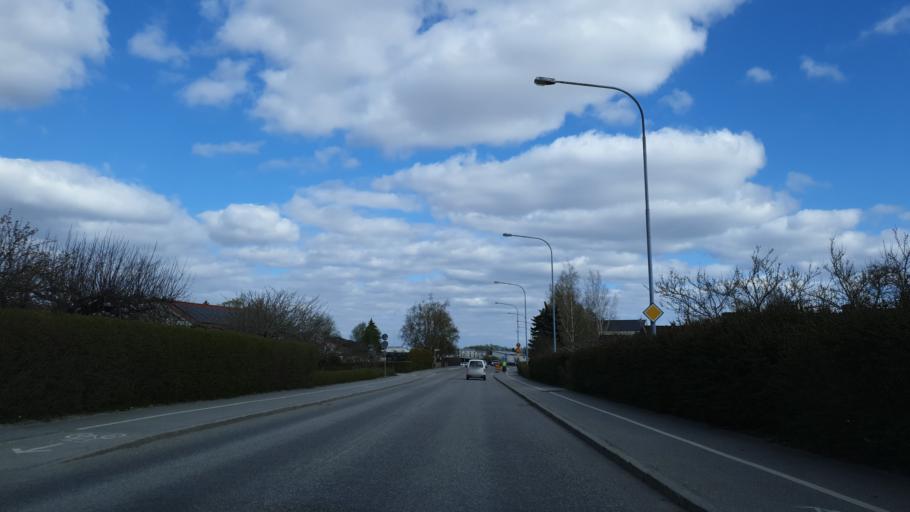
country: SE
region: Uppsala
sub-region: Uppsala Kommun
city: Gamla Uppsala
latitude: 59.8923
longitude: 17.6451
